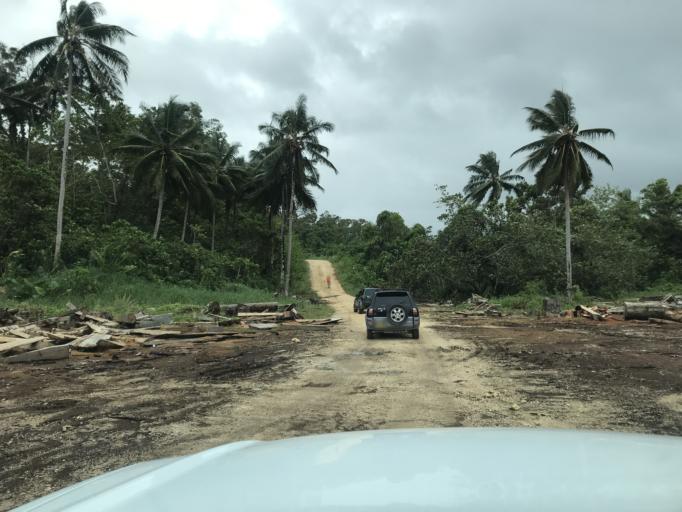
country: SB
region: Malaita
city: Auki
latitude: -8.6317
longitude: 160.6601
